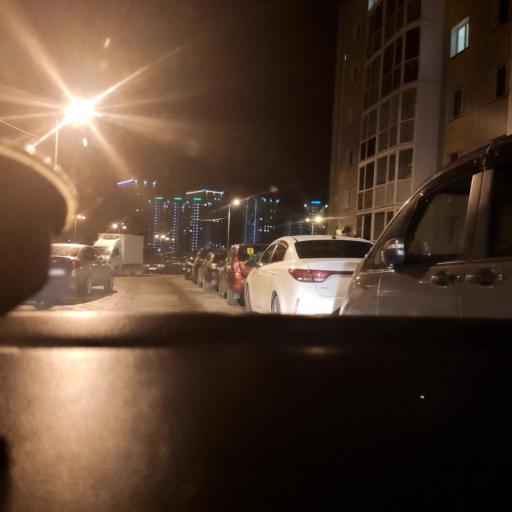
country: RU
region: Moskovskaya
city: Andreyevka
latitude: 55.9802
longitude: 37.1019
